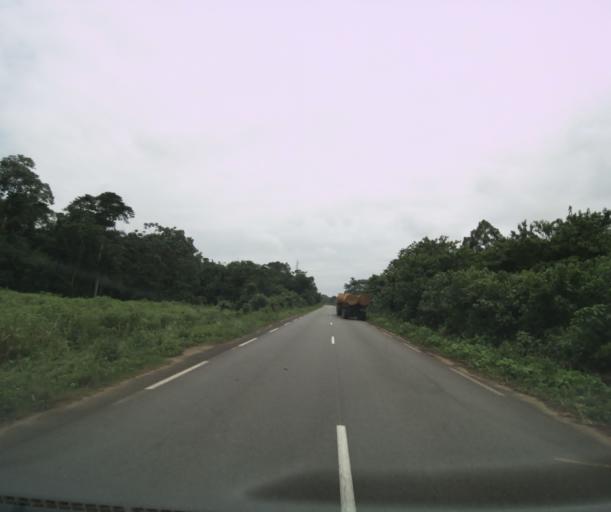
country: CM
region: South Province
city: Kribi
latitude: 3.1391
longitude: 10.0142
